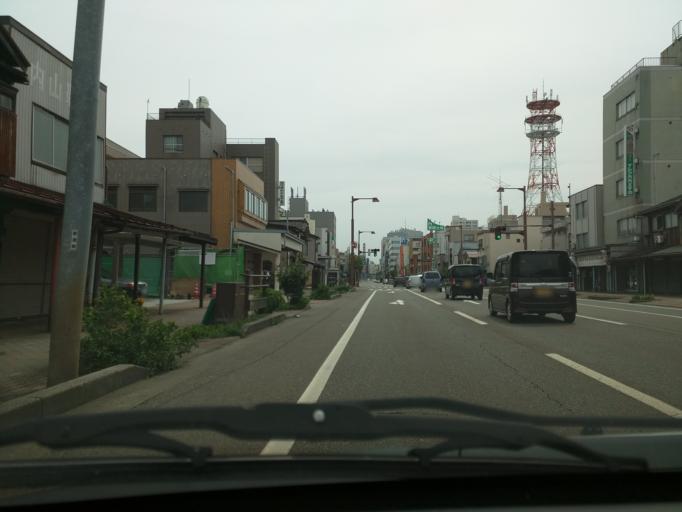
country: JP
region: Niigata
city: Nagaoka
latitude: 37.4526
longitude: 138.8526
